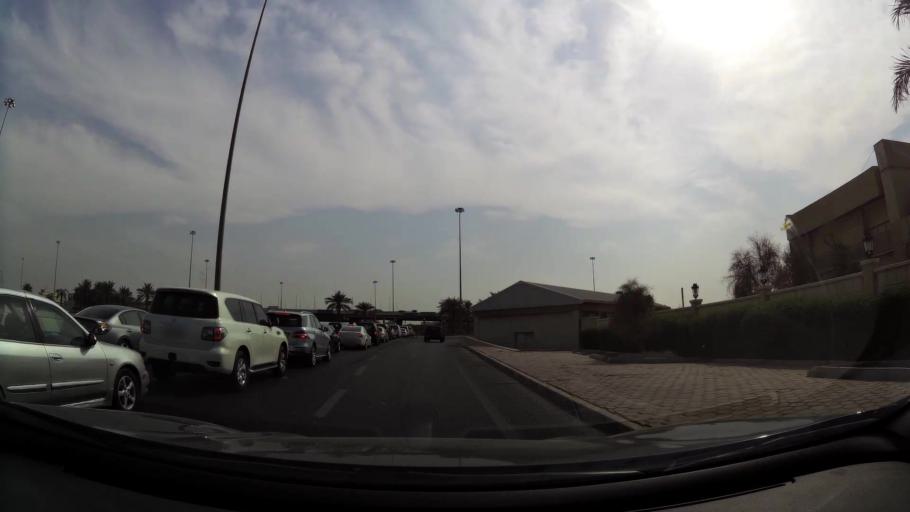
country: KW
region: Al Asimah
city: Ash Shamiyah
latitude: 29.3198
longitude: 47.9740
